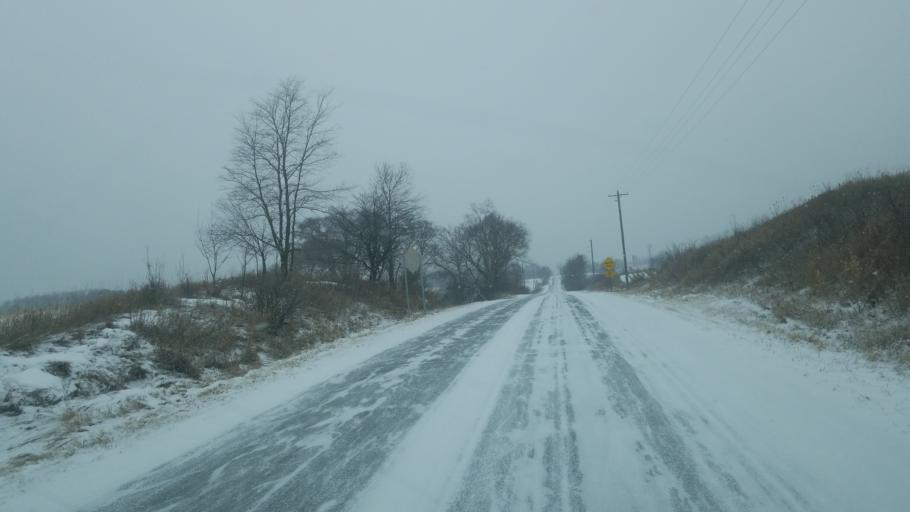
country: US
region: Michigan
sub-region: Mecosta County
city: Big Rapids
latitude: 43.7726
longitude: -85.4028
